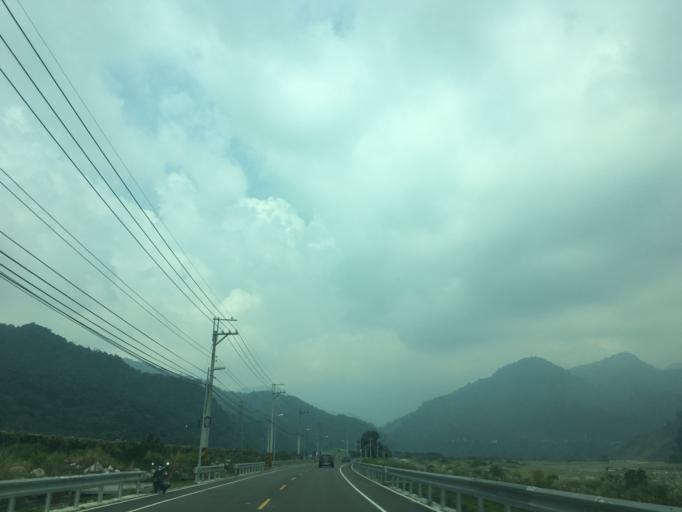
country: TW
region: Taiwan
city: Fengyuan
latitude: 24.2966
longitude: 120.8819
